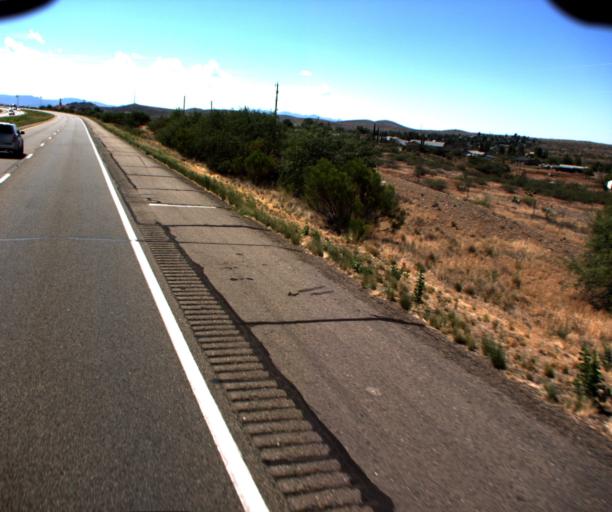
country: US
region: Arizona
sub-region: Yavapai County
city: Spring Valley
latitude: 34.3547
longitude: -112.1656
